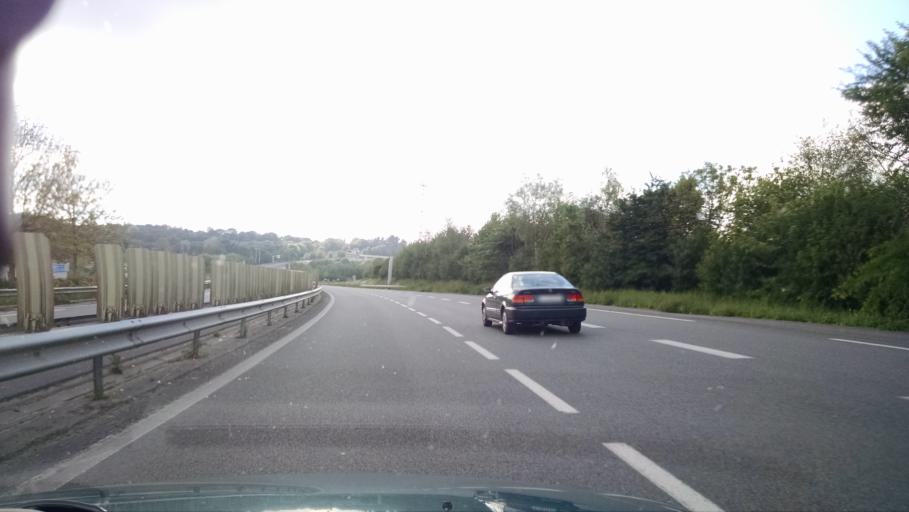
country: FR
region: Brittany
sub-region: Departement du Finistere
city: Morlaix
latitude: 48.5816
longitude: -3.8662
